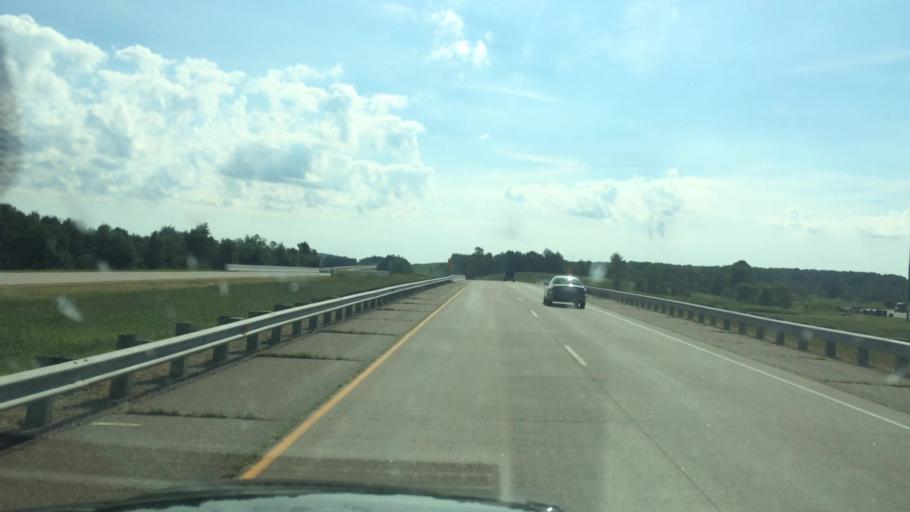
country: US
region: Wisconsin
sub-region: Shawano County
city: Wittenberg
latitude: 44.8233
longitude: -89.1247
